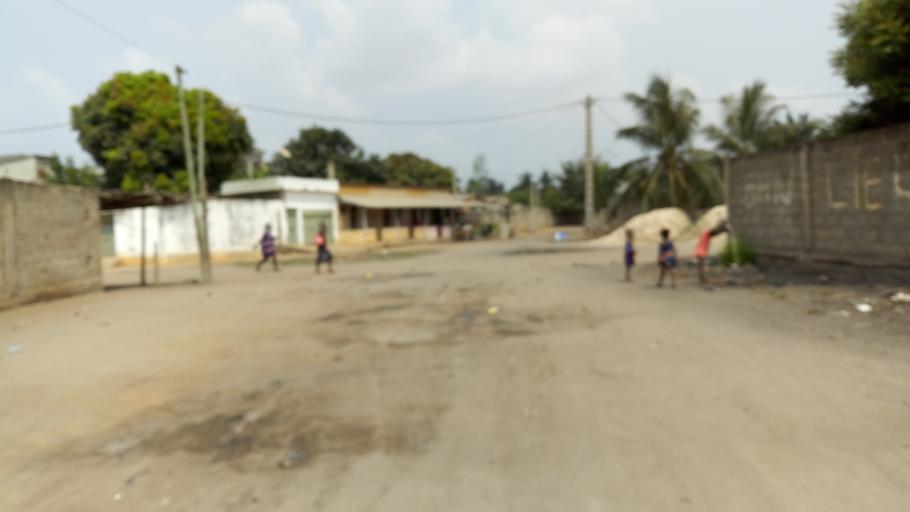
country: TG
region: Maritime
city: Lome
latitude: 6.1776
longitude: 1.1707
